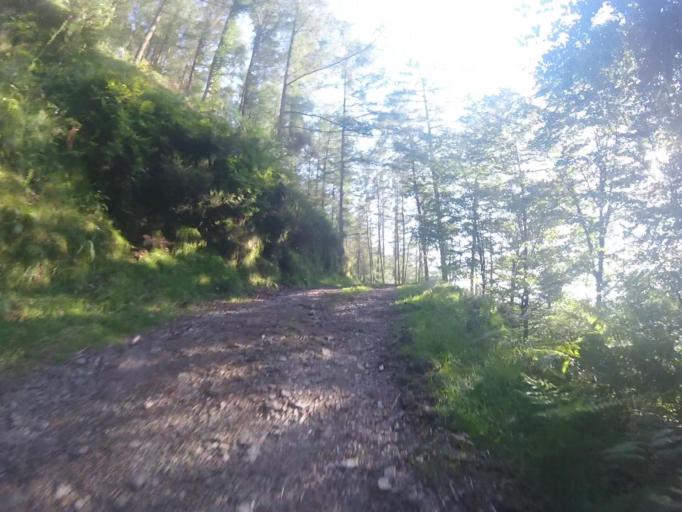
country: ES
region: Navarre
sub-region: Provincia de Navarra
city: Arano
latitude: 43.2444
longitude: -1.8517
